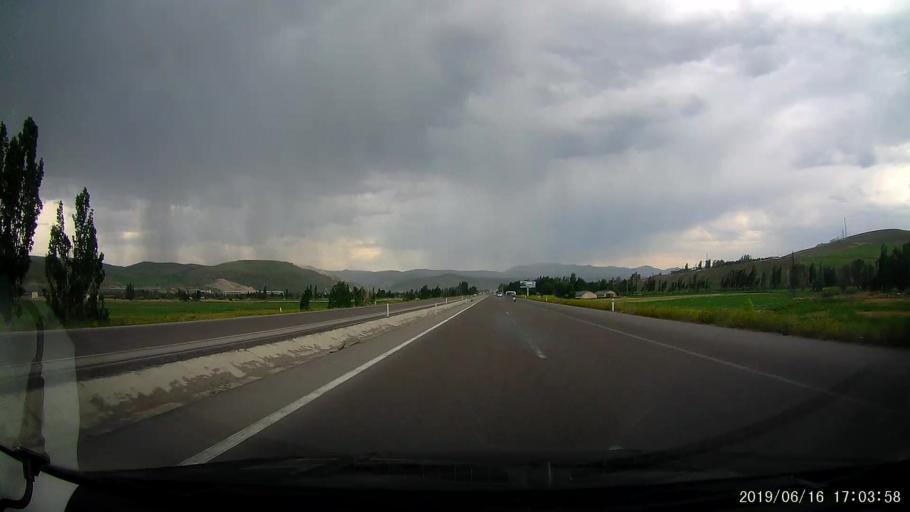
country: TR
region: Erzurum
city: Askale
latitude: 39.9311
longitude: 40.7196
